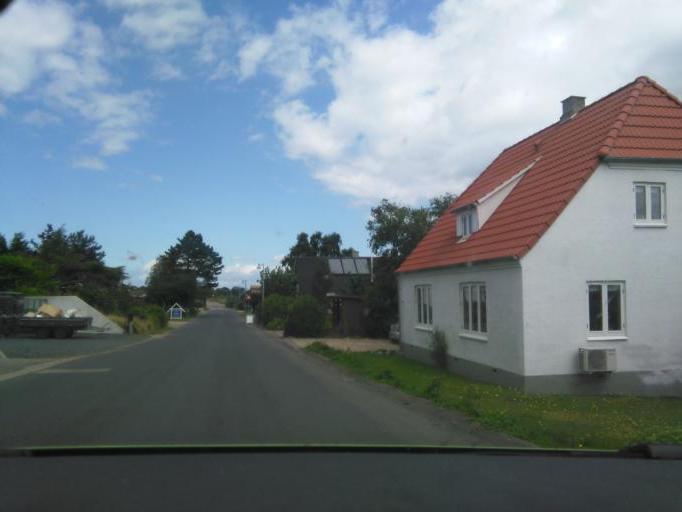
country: DK
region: Zealand
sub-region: Kalundborg Kommune
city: Gorlev
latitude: 55.5267
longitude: 11.1121
